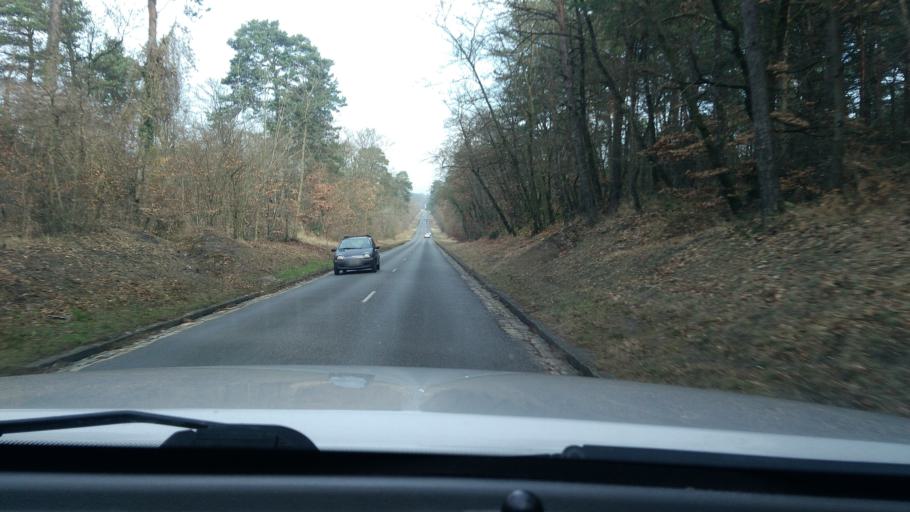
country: FR
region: Ile-de-France
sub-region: Departement de Seine-et-Marne
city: Avon
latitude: 48.4348
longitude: 2.7138
